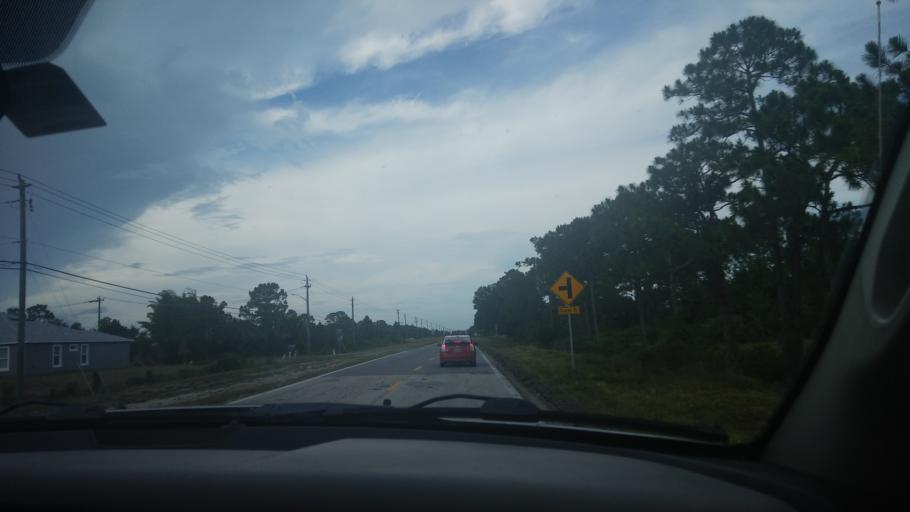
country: US
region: Florida
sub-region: Brevard County
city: Grant-Valkaria
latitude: 27.9153
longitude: -80.6229
